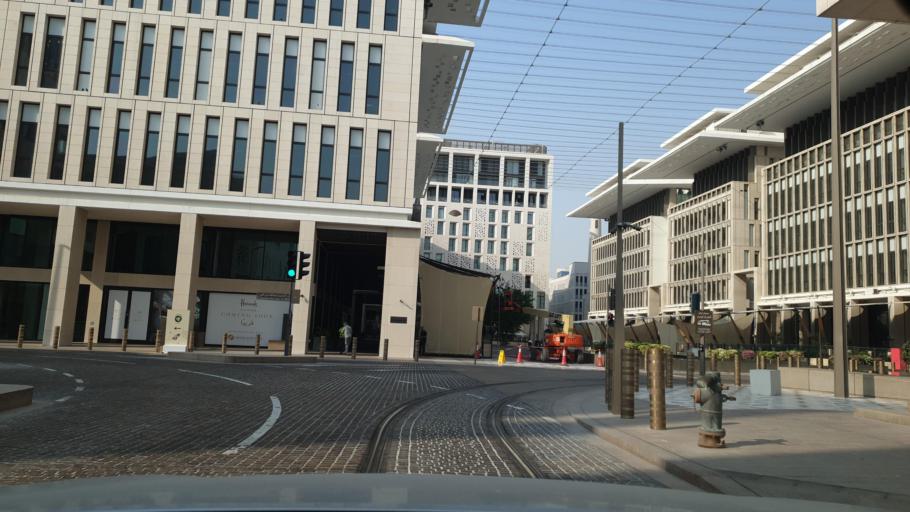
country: QA
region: Baladiyat ad Dawhah
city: Doha
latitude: 25.2865
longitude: 51.5277
